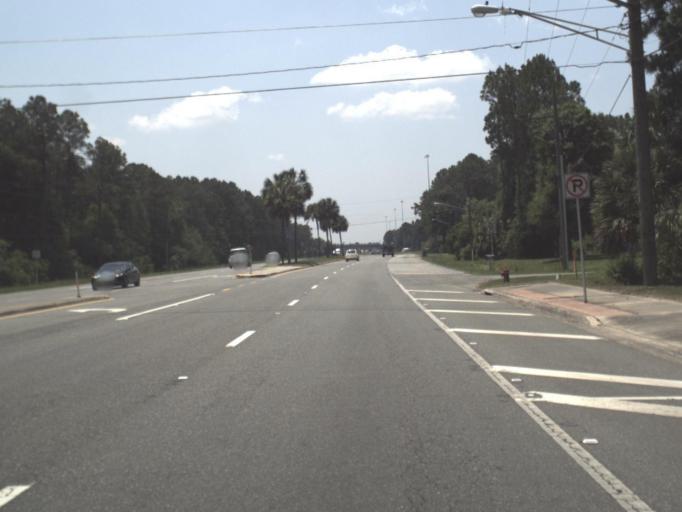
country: US
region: Florida
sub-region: Duval County
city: Baldwin
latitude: 30.2959
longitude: -81.9830
